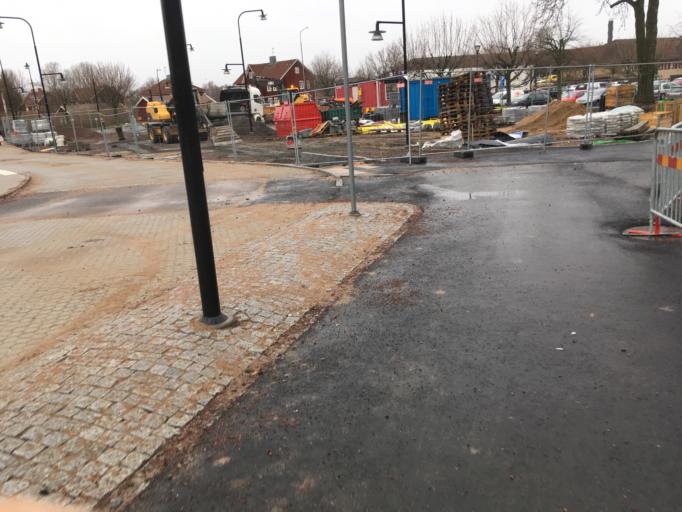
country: SE
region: Vaermland
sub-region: Hammaro Kommun
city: Skoghall
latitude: 59.3232
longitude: 13.4661
